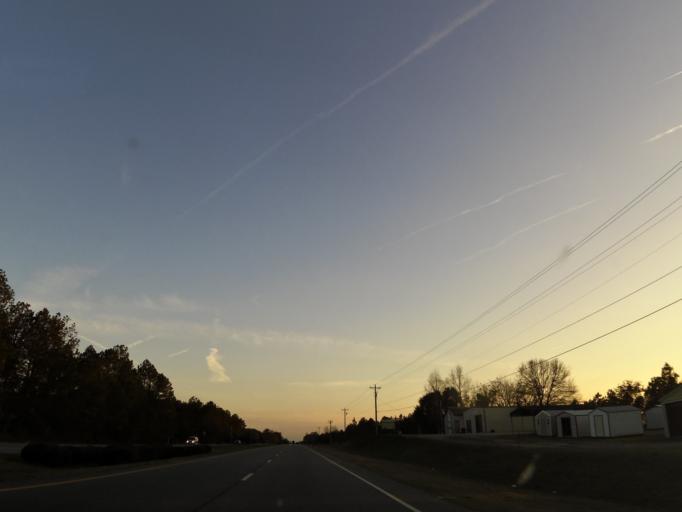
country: US
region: Georgia
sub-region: Lee County
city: Leesburg
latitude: 31.7150
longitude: -84.1726
